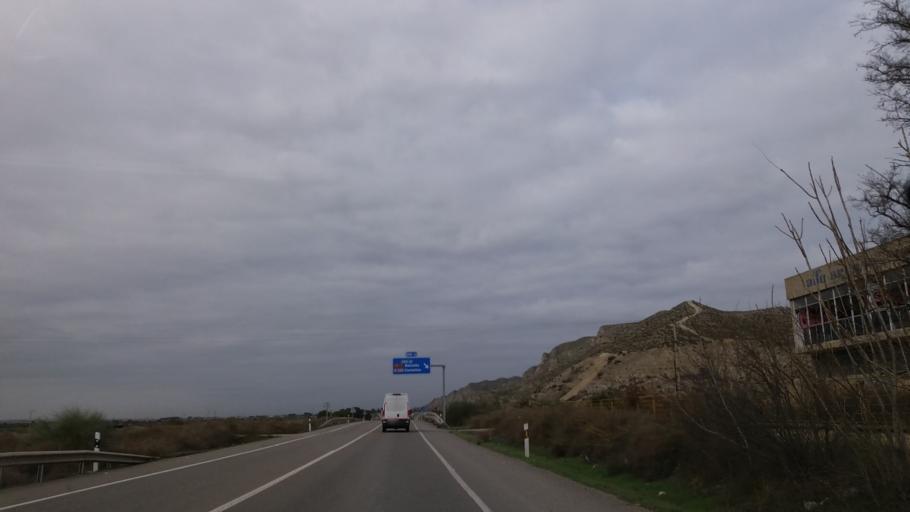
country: ES
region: Aragon
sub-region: Provincia de Zaragoza
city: Villafranca de Ebro
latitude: 41.5773
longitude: -0.6475
